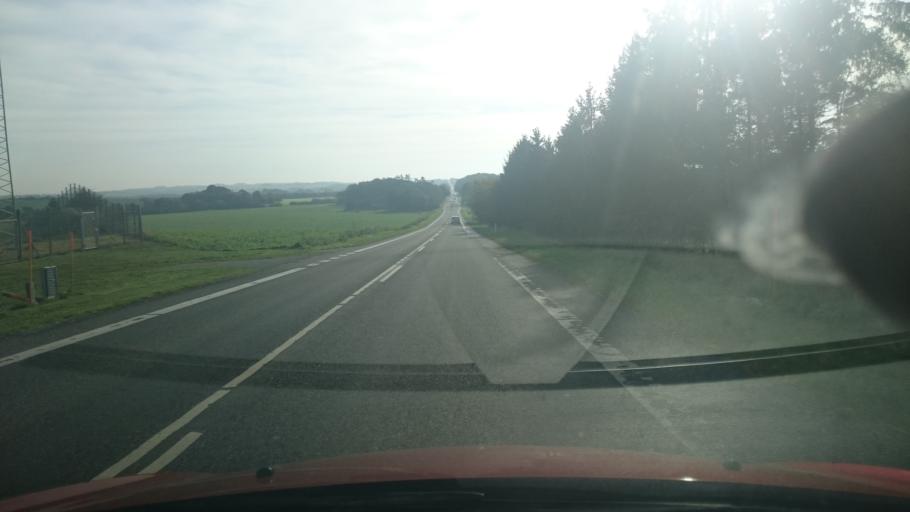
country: DK
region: Central Jutland
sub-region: Randers Kommune
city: Assentoft
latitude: 56.4107
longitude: 10.2269
